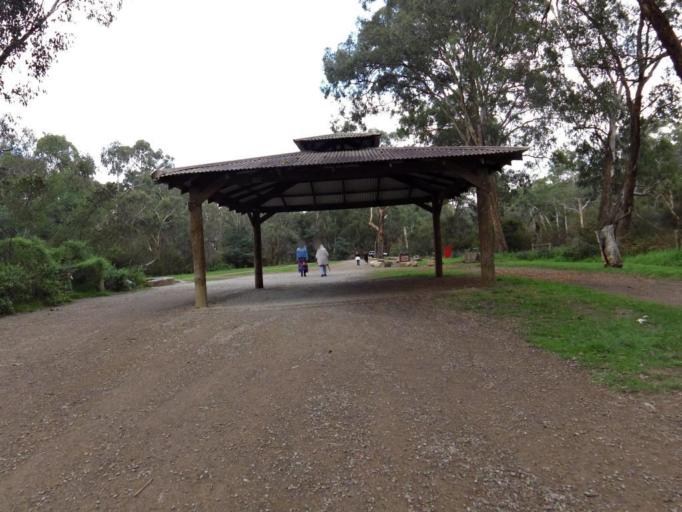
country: AU
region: Victoria
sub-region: Nillumbik
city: North Warrandyte
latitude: -37.7406
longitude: 145.2108
